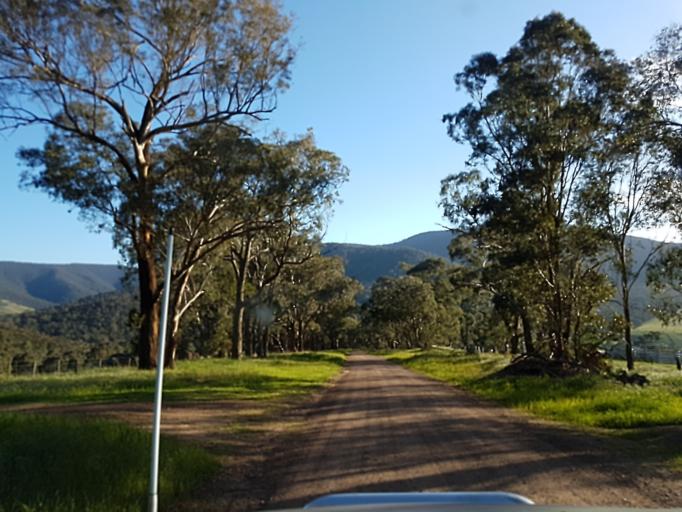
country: AU
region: Victoria
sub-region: East Gippsland
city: Bairnsdale
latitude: -37.4899
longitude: 147.1897
